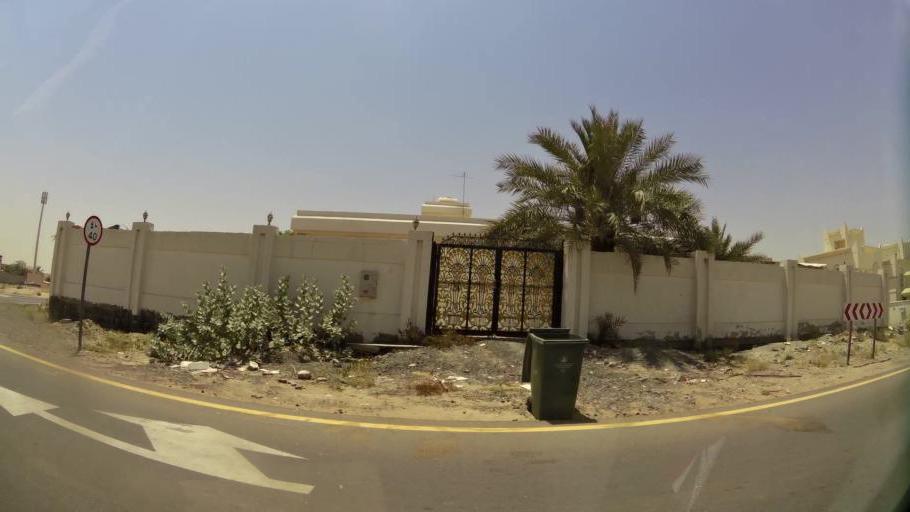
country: AE
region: Ajman
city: Ajman
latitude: 25.4030
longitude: 55.5173
